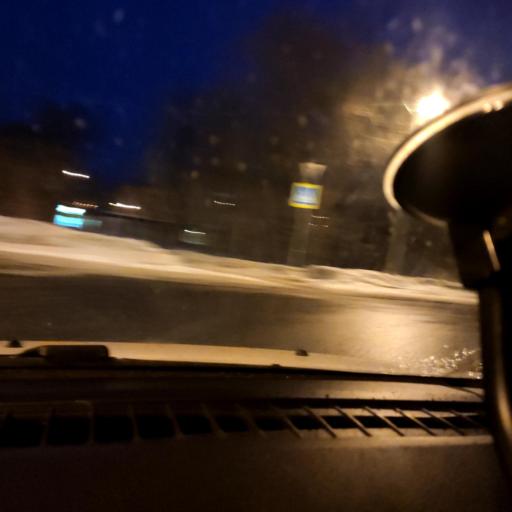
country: RU
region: Samara
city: Bereza
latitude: 53.5142
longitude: 50.1420
